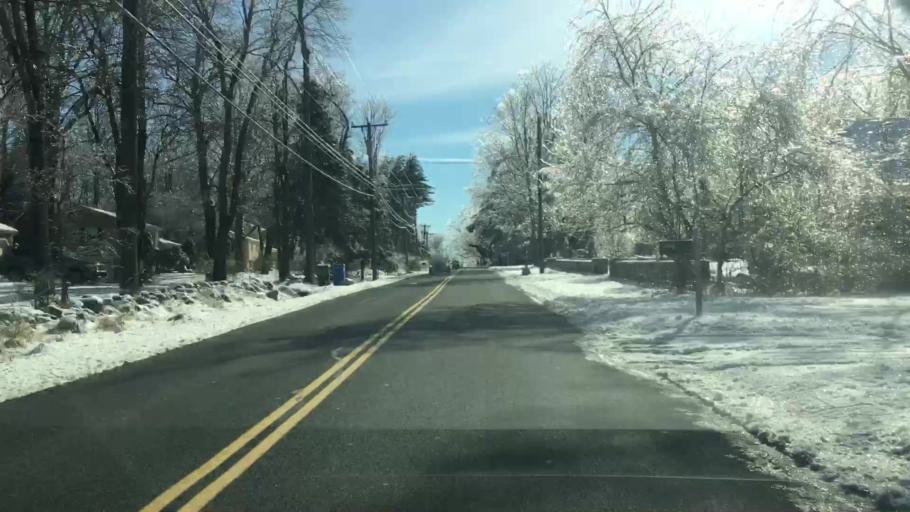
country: US
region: Connecticut
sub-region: Fairfield County
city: Trumbull
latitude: 41.3263
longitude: -73.2215
